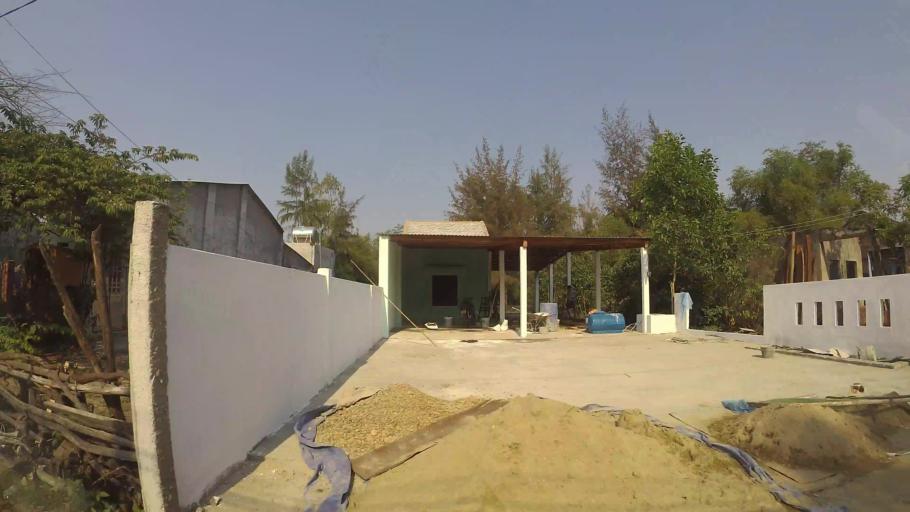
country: VN
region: Da Nang
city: Ngu Hanh Son
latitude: 15.9587
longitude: 108.2641
